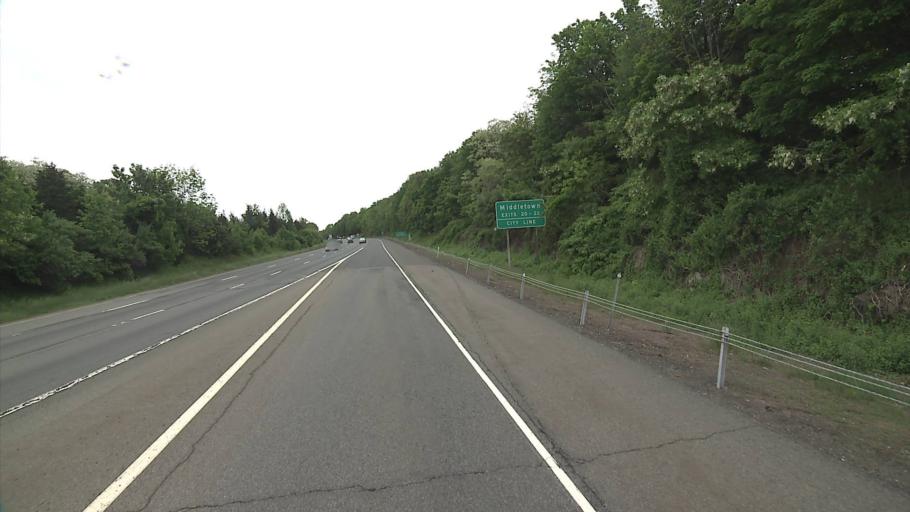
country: US
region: Connecticut
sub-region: New Haven County
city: Meriden
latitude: 41.5451
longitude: -72.7494
